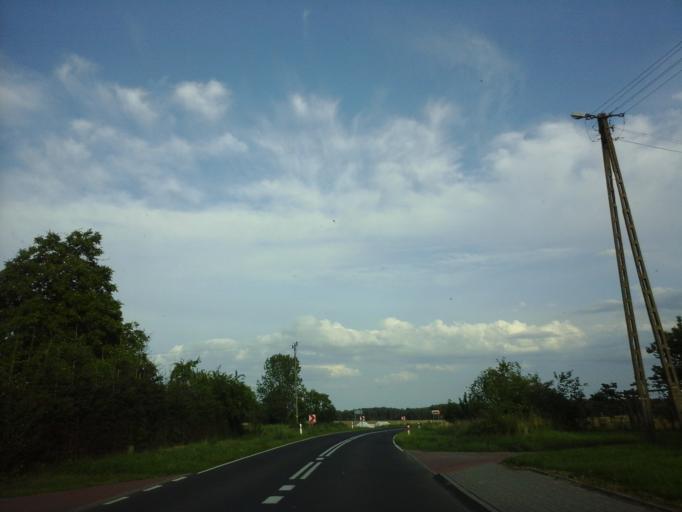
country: PL
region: West Pomeranian Voivodeship
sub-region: Powiat kamienski
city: Kamien Pomorski
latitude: 53.9257
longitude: 14.8390
